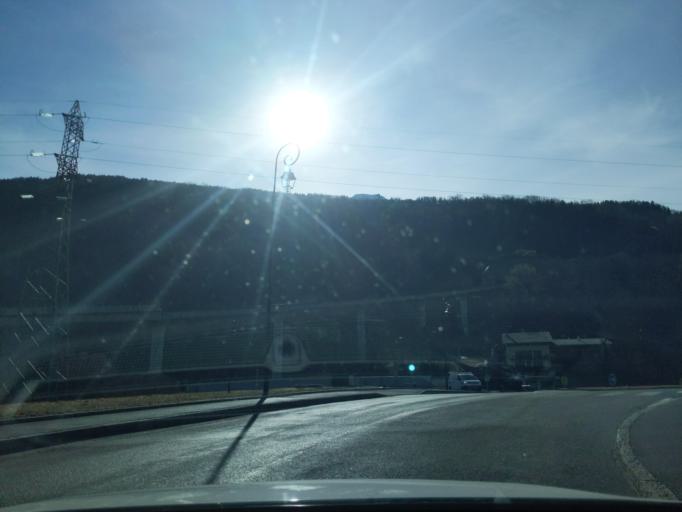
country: FR
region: Rhone-Alpes
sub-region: Departement de la Savoie
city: Bourg-Saint-Maurice
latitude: 45.6122
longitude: 6.7731
